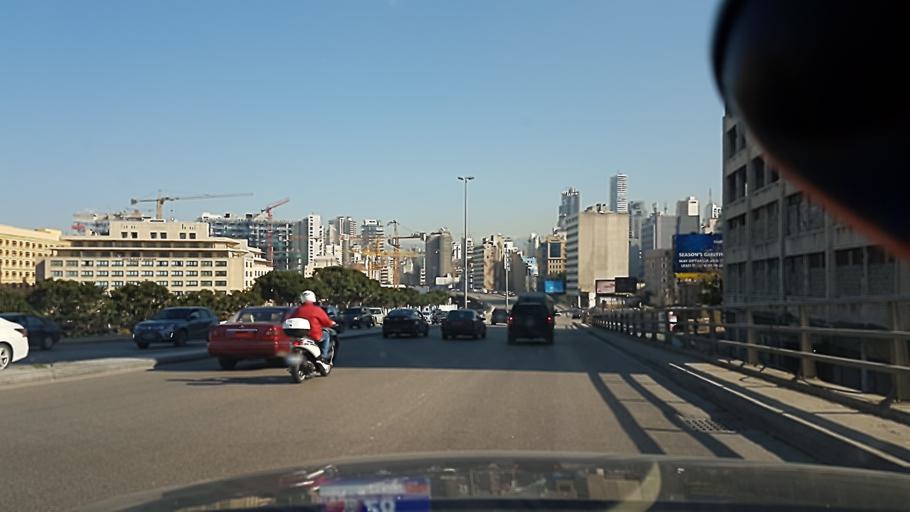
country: LB
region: Beyrouth
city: Beirut
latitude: 33.8931
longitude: 35.5023
